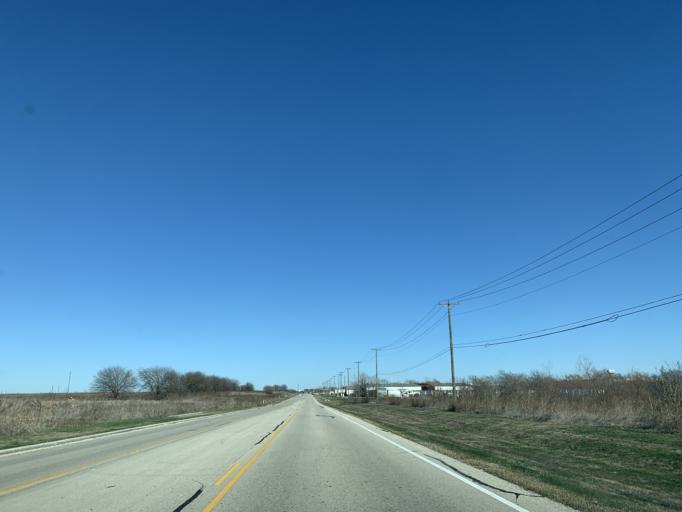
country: US
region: Texas
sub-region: Williamson County
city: Hutto
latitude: 30.5429
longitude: -97.5737
